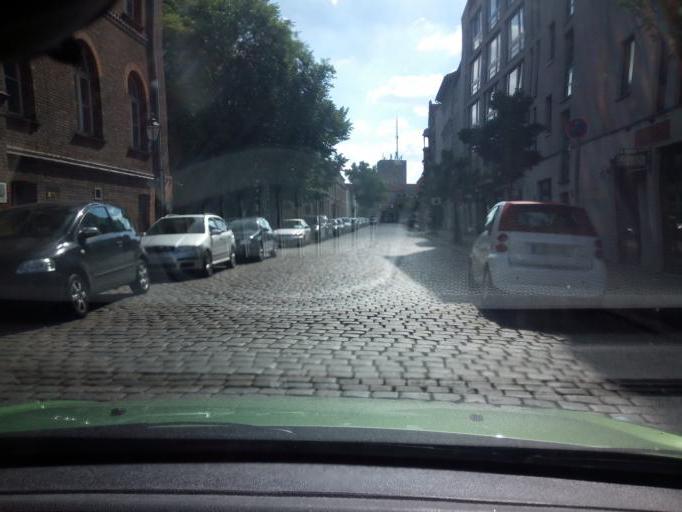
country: DE
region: Berlin
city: Kopenick Bezirk
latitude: 52.4474
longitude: 13.5760
